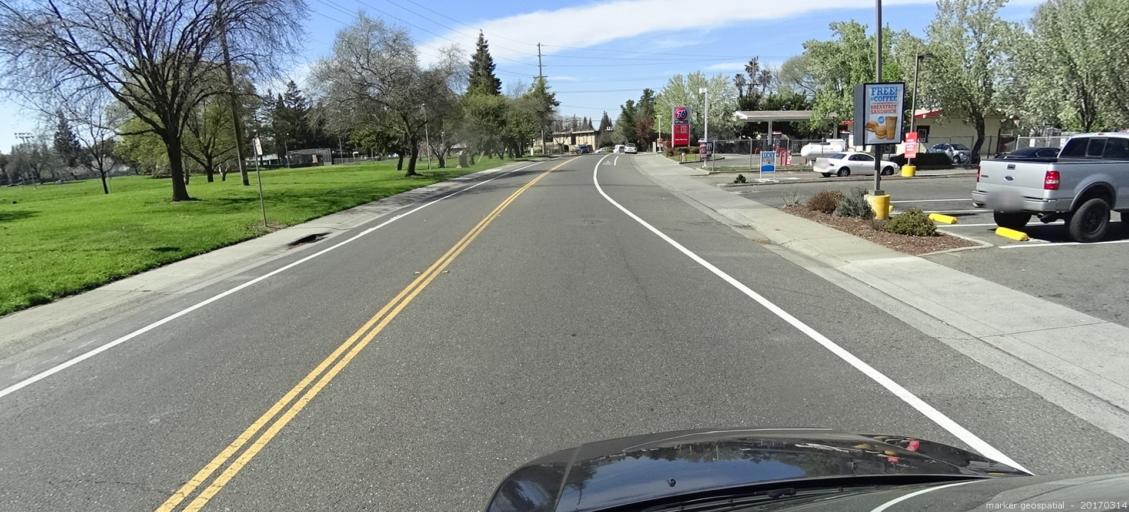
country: US
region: California
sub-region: Sacramento County
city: Parkway
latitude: 38.5162
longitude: -121.5152
